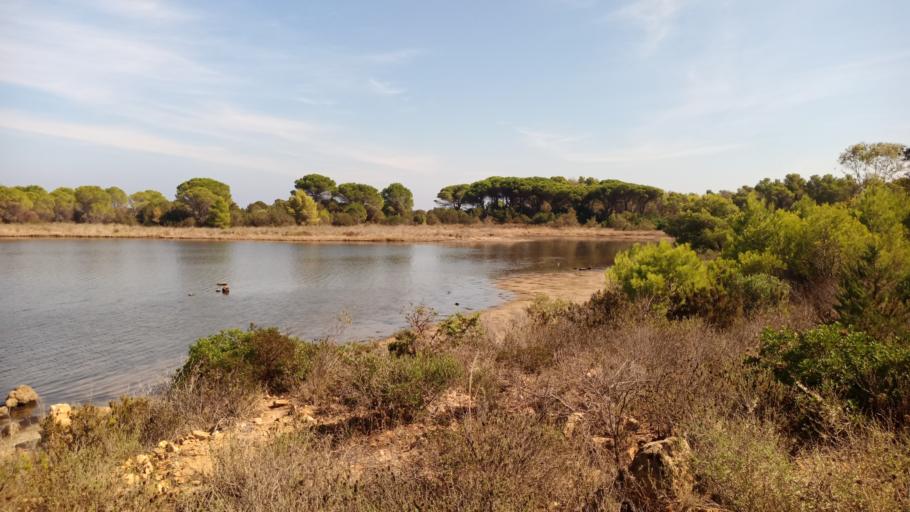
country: IT
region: Sardinia
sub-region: Provincia di Nuoro
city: Orosei
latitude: 40.4622
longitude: 9.7991
